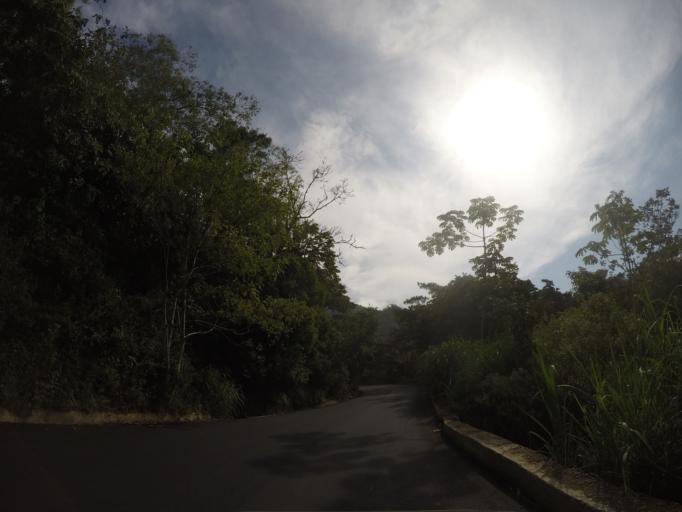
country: MX
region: Oaxaca
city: Pluma Hidalgo
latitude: 15.9324
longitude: -96.4272
